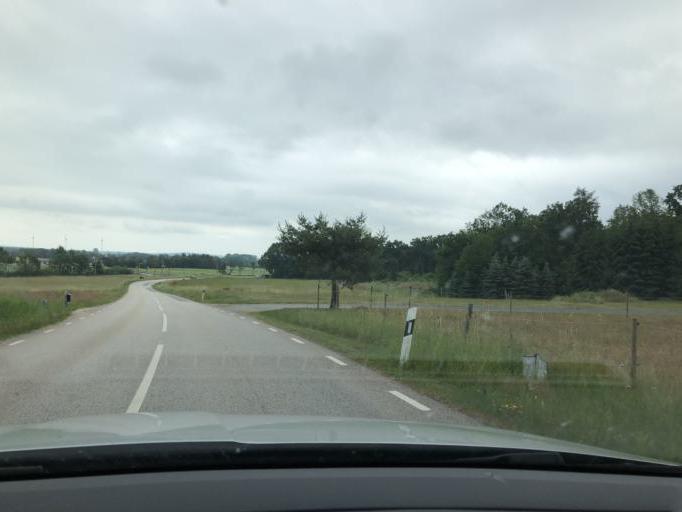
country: SE
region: Blekinge
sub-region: Solvesborgs Kommun
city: Soelvesborg
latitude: 56.0768
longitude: 14.6089
